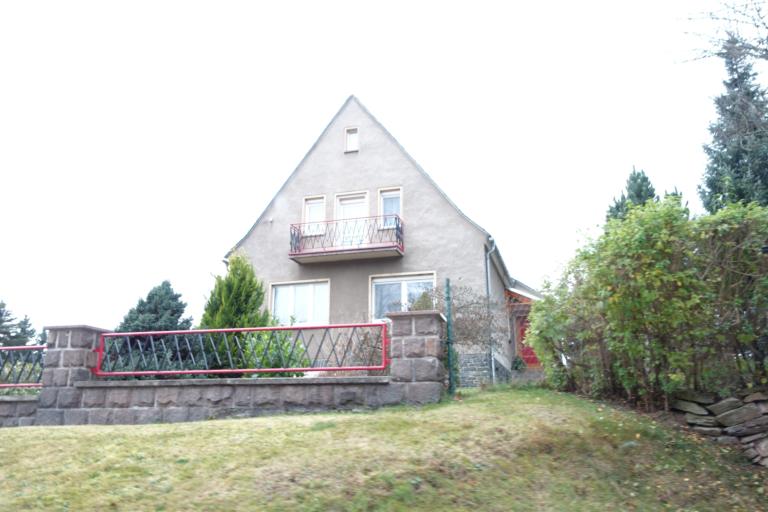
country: DE
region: Saxony
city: Eppendorf
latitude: 50.8121
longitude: 13.2528
